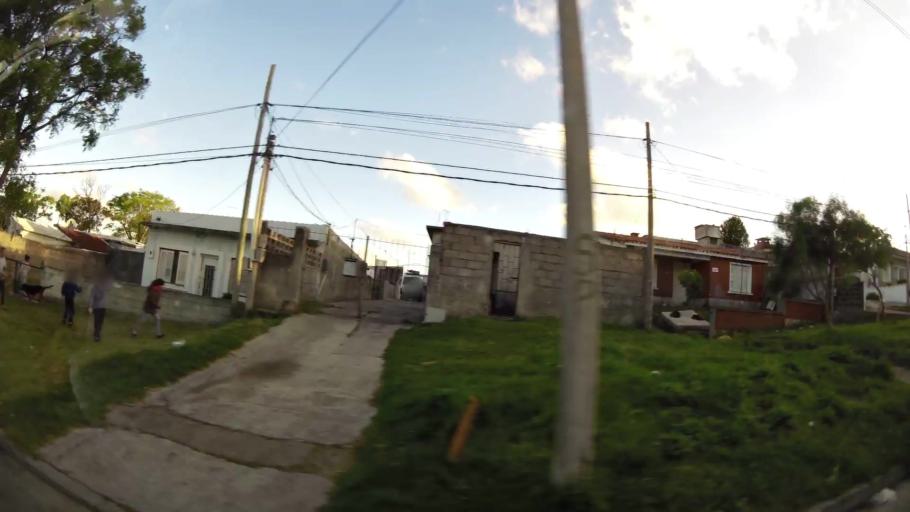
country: UY
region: Montevideo
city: Montevideo
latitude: -34.8839
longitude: -56.2553
